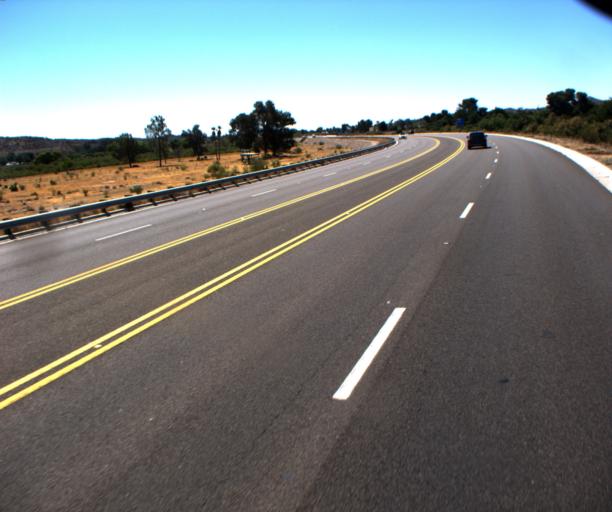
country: US
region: Arizona
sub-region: Maricopa County
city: Wickenburg
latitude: 33.9769
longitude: -112.7330
